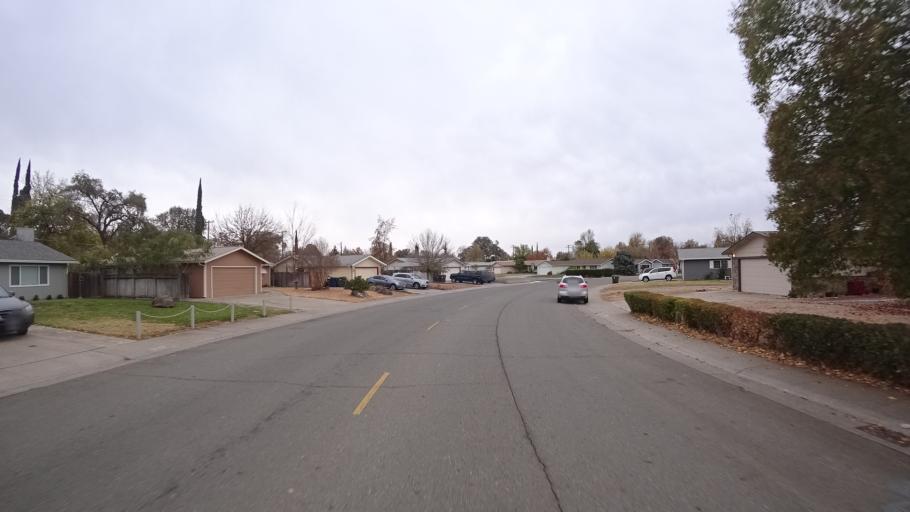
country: US
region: California
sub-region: Sacramento County
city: Citrus Heights
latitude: 38.6983
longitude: -121.3032
